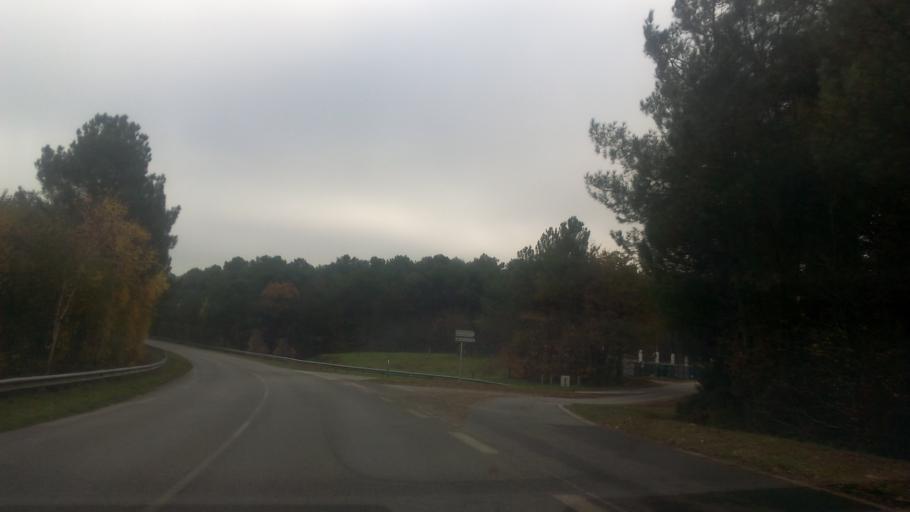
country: FR
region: Brittany
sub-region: Departement du Morbihan
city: Saint-Vincent-sur-Oust
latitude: 47.6846
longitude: -2.1384
